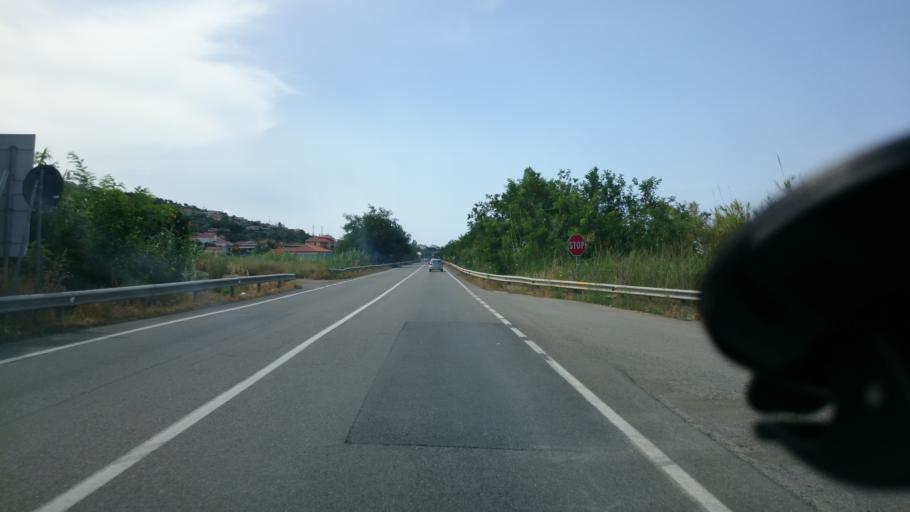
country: IT
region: Calabria
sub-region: Provincia di Cosenza
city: Diamante
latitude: 39.7098
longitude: 15.8136
